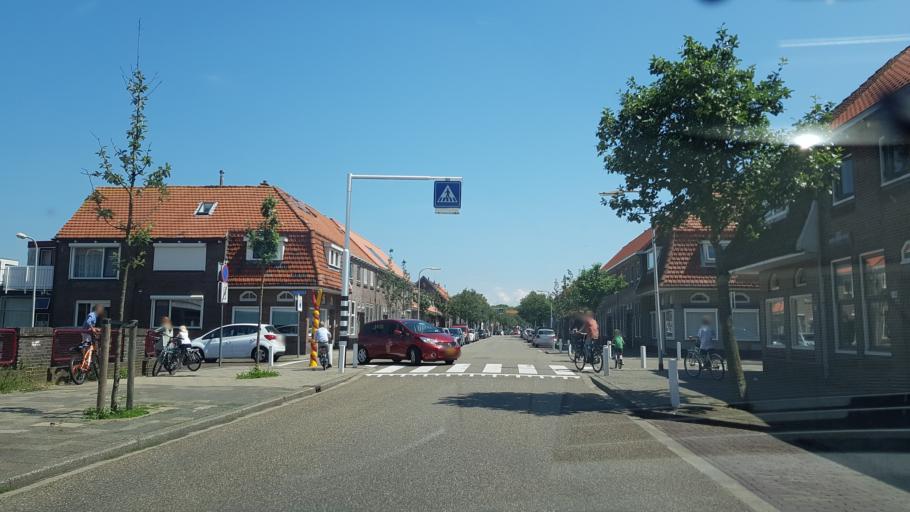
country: NL
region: South Holland
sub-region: Gemeente Katwijk
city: Katwijk aan Zee
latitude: 52.2012
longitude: 4.3995
